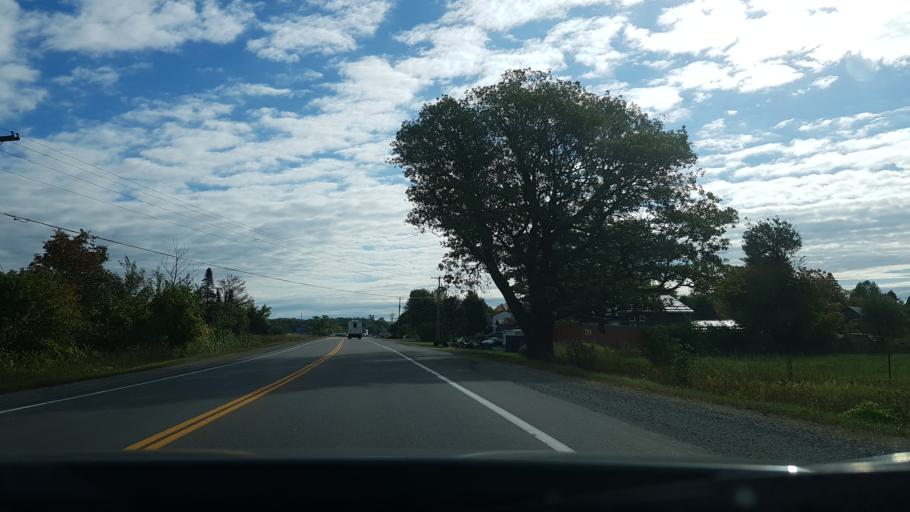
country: CA
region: Ontario
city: Orillia
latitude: 44.6151
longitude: -79.4966
